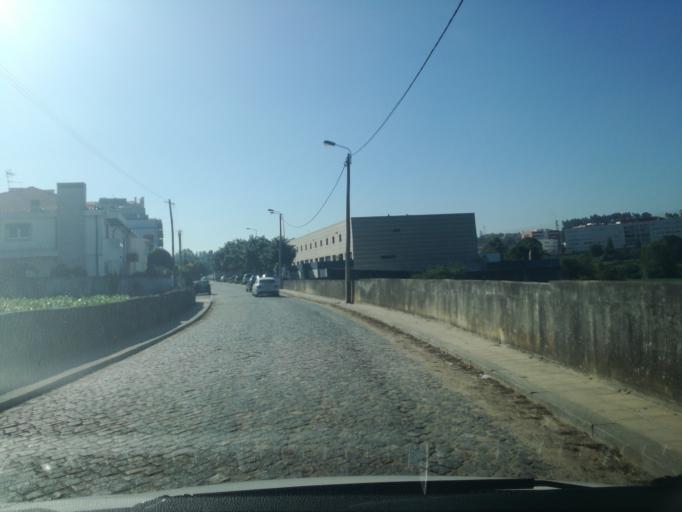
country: PT
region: Porto
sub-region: Maia
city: Leca do Bailio
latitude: 41.2077
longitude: -8.6164
